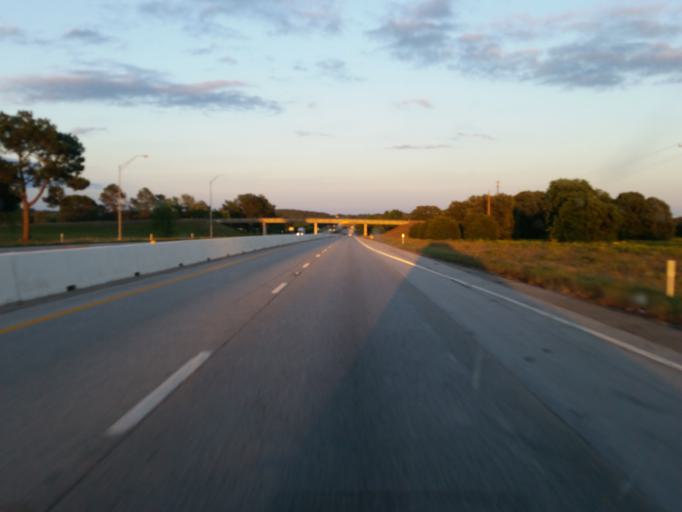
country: US
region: Texas
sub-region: Van Zandt County
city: Van
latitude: 32.4917
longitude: -95.5553
